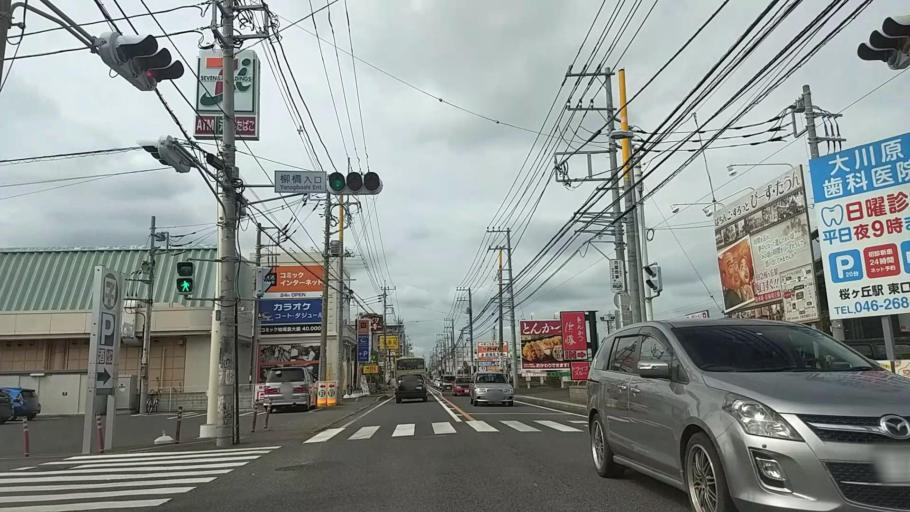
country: JP
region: Kanagawa
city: Minami-rinkan
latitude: 35.4557
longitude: 139.4669
